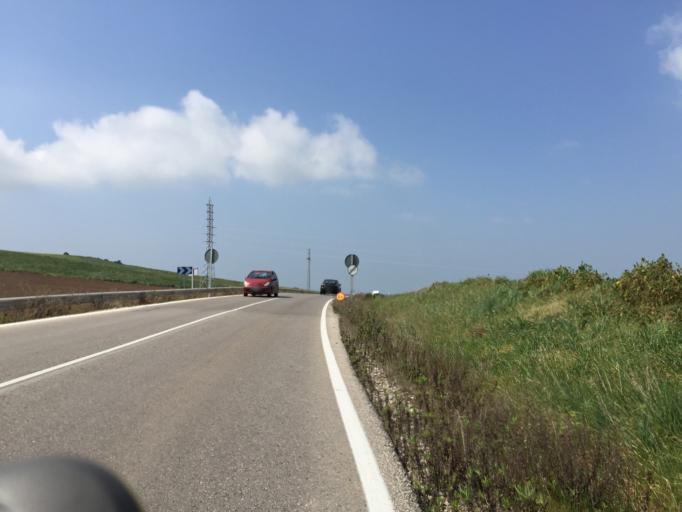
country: ES
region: Andalusia
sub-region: Provincia de Cadiz
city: Vejer de la Frontera
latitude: 36.2364
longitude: -6.0087
